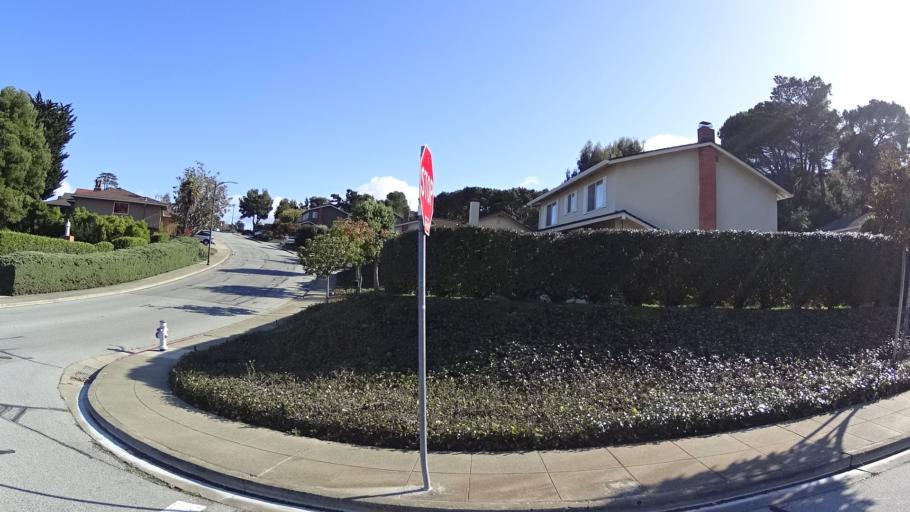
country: US
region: California
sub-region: San Mateo County
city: Hillsborough
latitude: 37.5822
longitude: -122.3961
